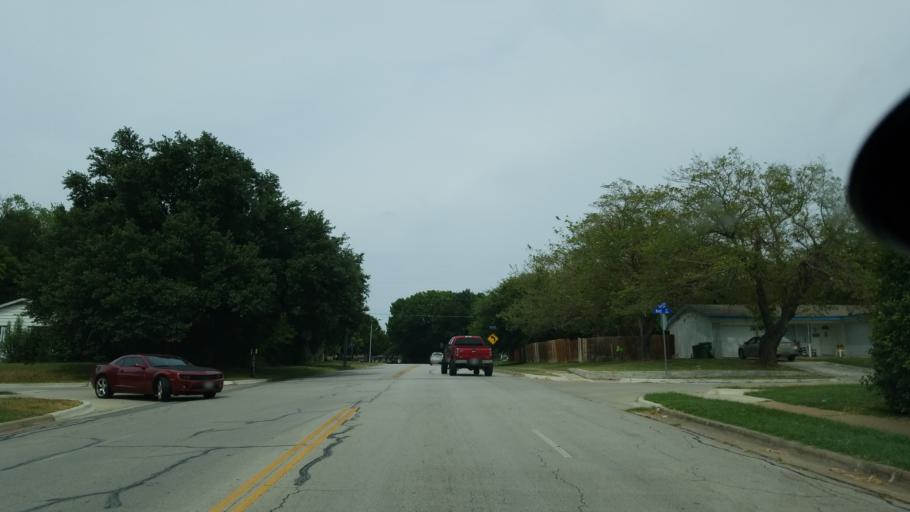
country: US
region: Texas
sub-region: Tarrant County
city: Arlington
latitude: 32.7165
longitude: -97.0847
